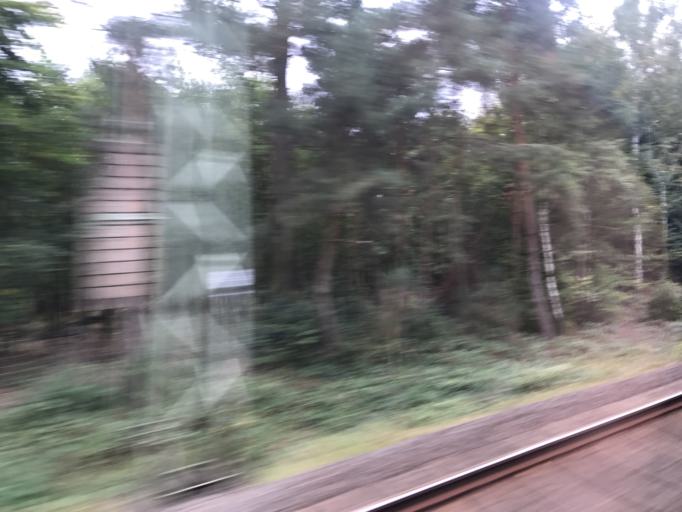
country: DE
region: Hesse
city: Kelsterbach
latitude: 50.0620
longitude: 8.5512
